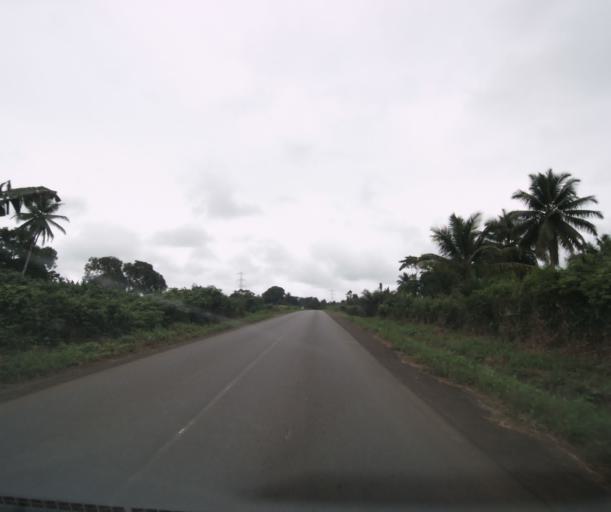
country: CM
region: Littoral
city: Edea
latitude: 3.7139
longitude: 10.1082
